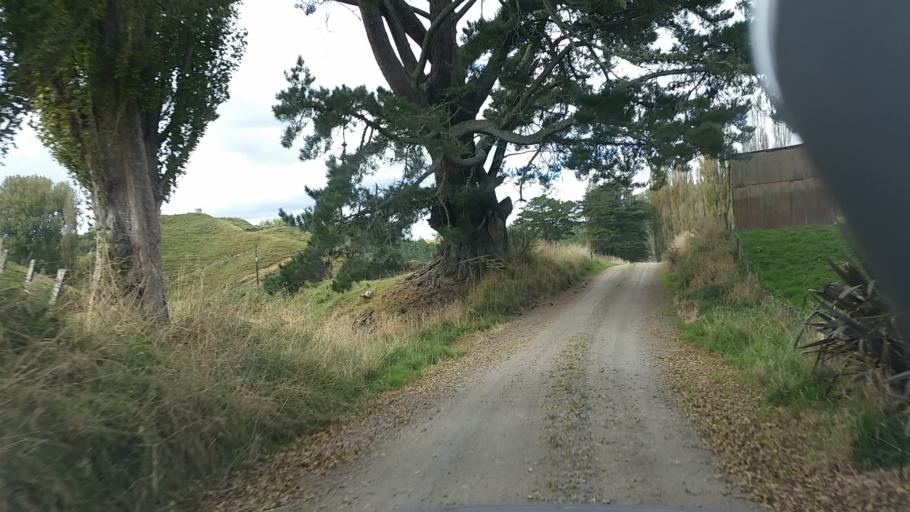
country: NZ
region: Taranaki
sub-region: South Taranaki District
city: Eltham
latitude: -39.2592
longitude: 174.5562
